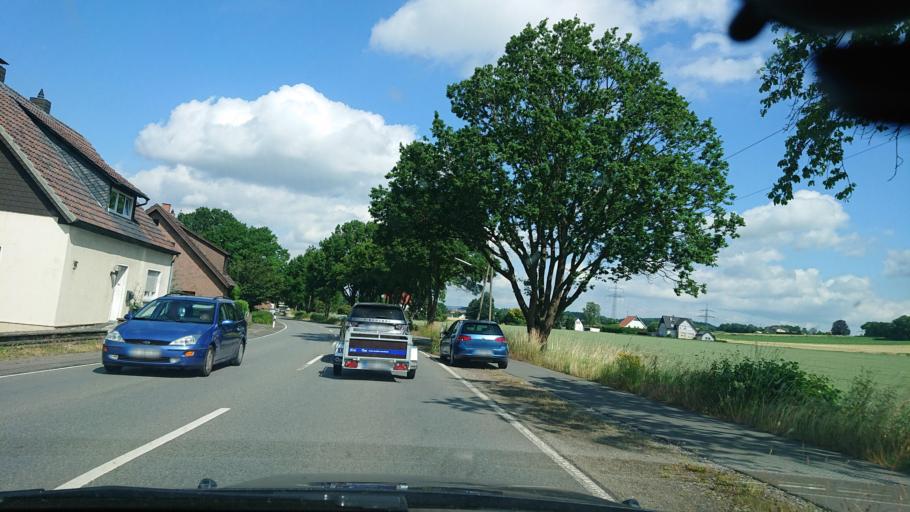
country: DE
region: North Rhine-Westphalia
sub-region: Regierungsbezirk Detmold
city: Hiddenhausen
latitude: 52.1576
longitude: 8.6422
